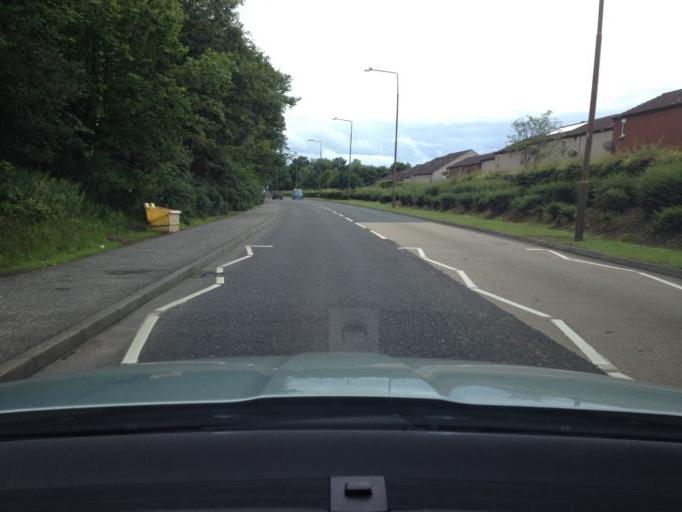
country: GB
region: Scotland
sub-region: West Lothian
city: Livingston
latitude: 55.8962
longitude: -3.5331
